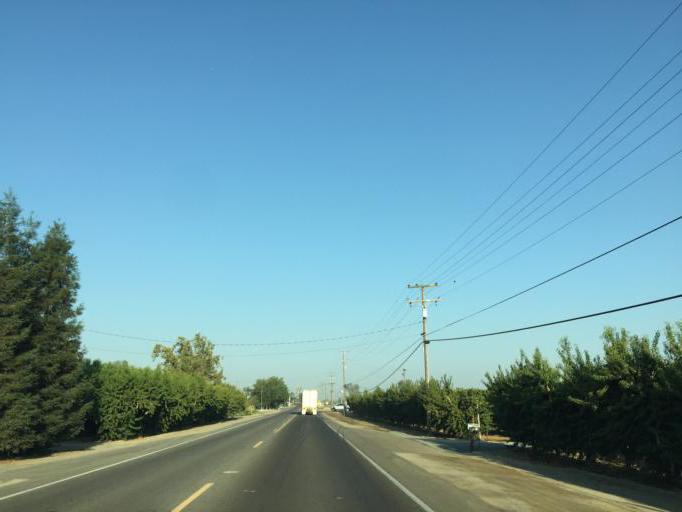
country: US
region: California
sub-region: Fresno County
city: Kingsburg
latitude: 36.4888
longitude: -119.5099
